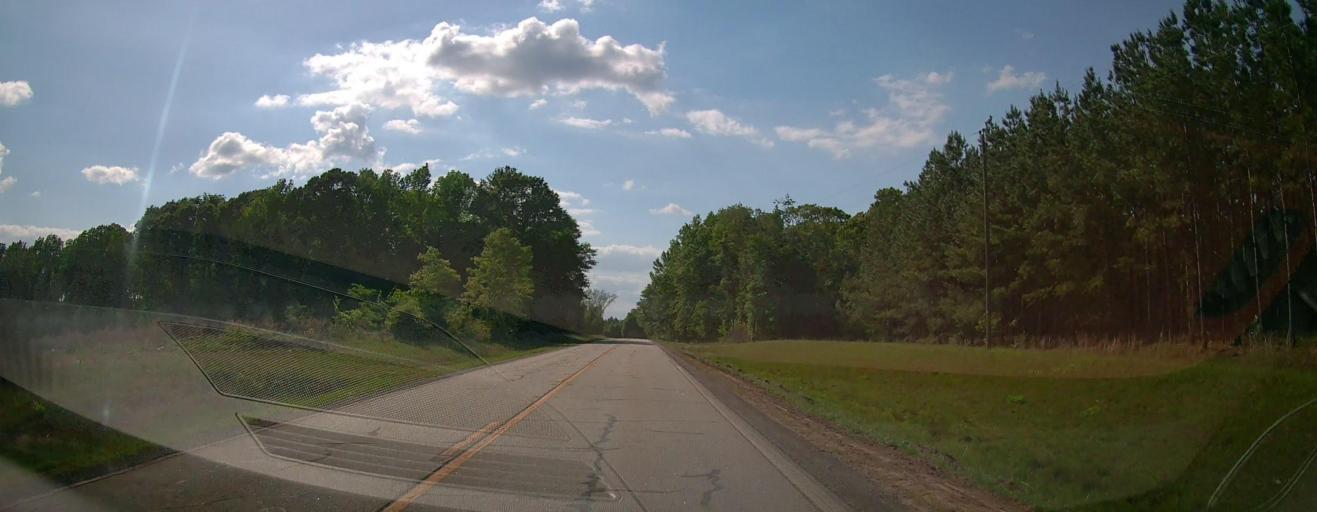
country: US
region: Georgia
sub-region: Washington County
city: Tennille
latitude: 32.9173
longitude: -82.9934
